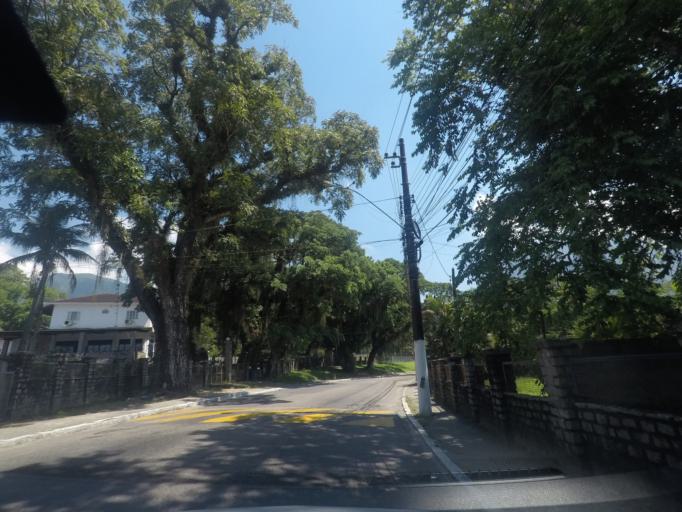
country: BR
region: Rio de Janeiro
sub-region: Petropolis
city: Petropolis
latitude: -22.5782
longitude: -43.1877
